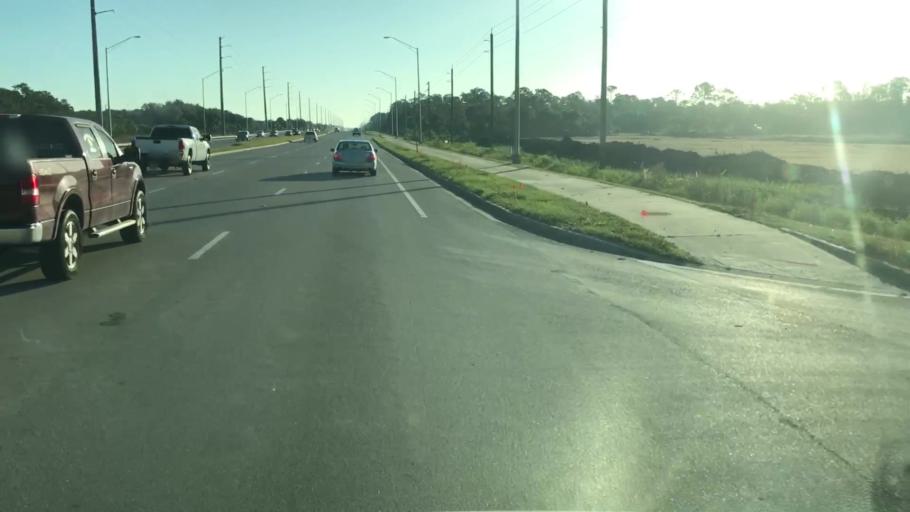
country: US
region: Florida
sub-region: Collier County
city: Orangetree
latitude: 26.2739
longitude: -81.6451
